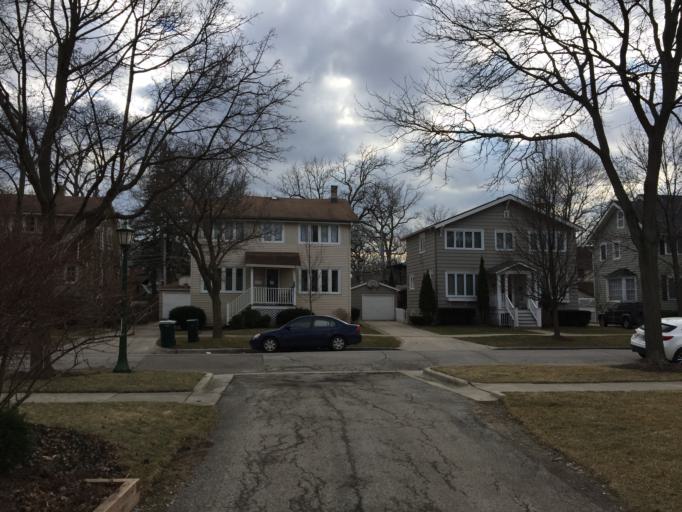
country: US
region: Illinois
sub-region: Cook County
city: Wilmette
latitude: 42.0728
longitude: -87.7101
